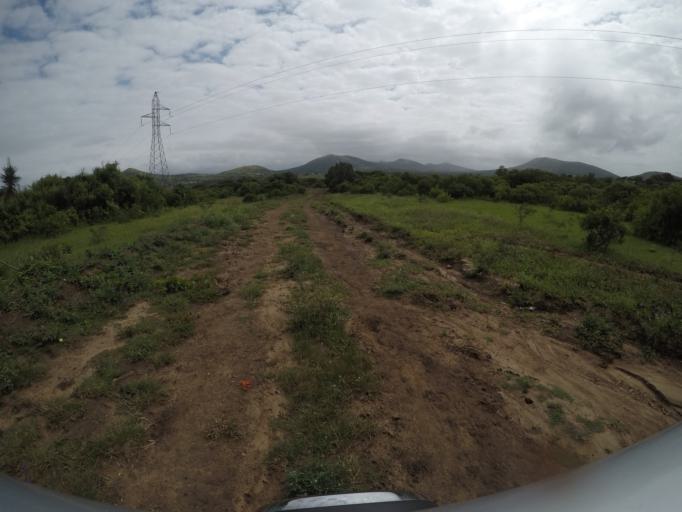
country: ZA
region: KwaZulu-Natal
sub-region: uThungulu District Municipality
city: Empangeni
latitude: -28.6236
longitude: 31.8650
